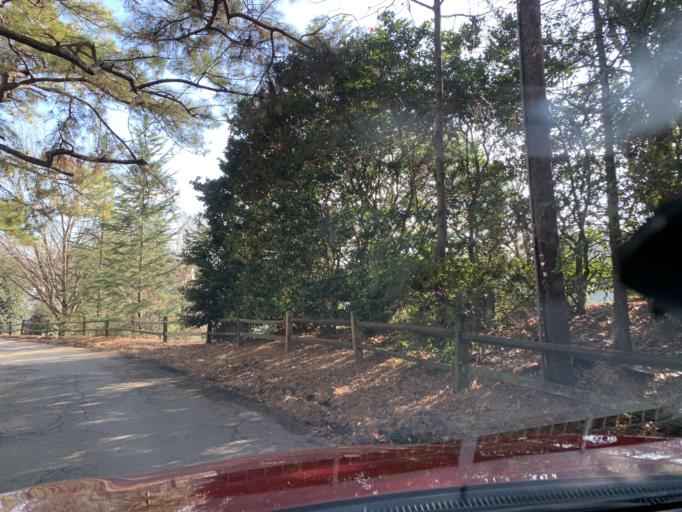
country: US
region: Georgia
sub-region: DeKalb County
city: Druid Hills
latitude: 33.8019
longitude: -84.3774
